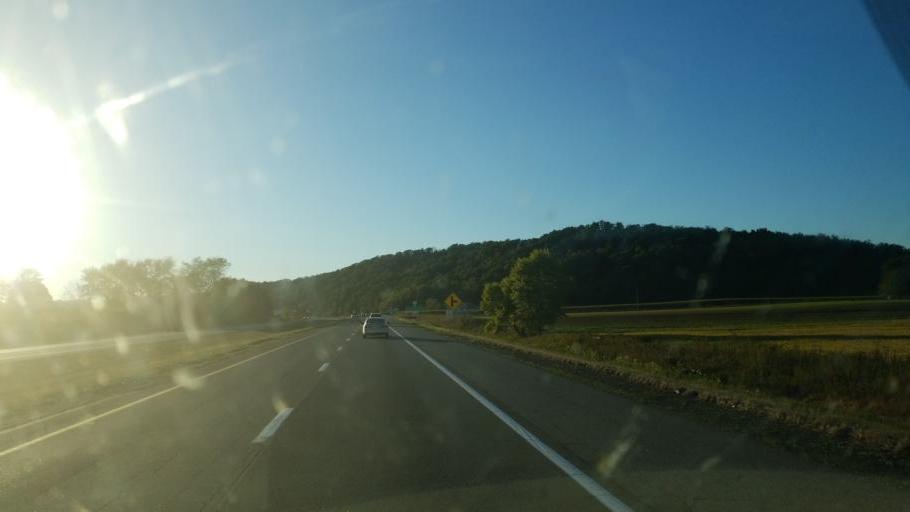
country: US
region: Ohio
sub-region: Coshocton County
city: Coshocton
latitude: 40.3013
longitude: -81.8311
